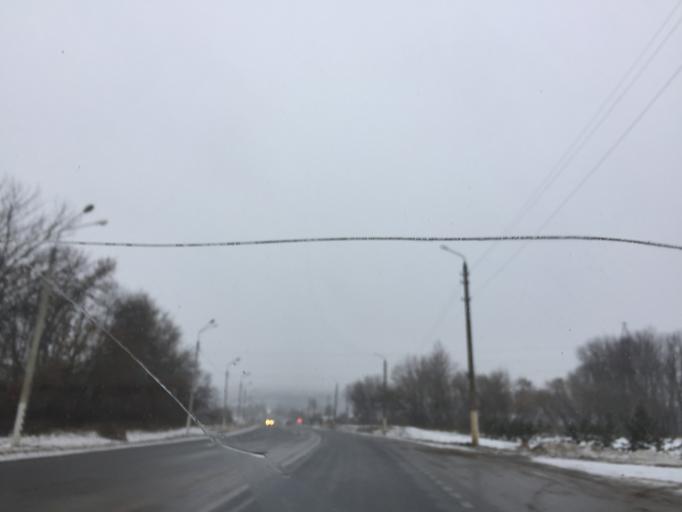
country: RU
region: Tula
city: Plavsk
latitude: 53.7238
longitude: 37.3000
